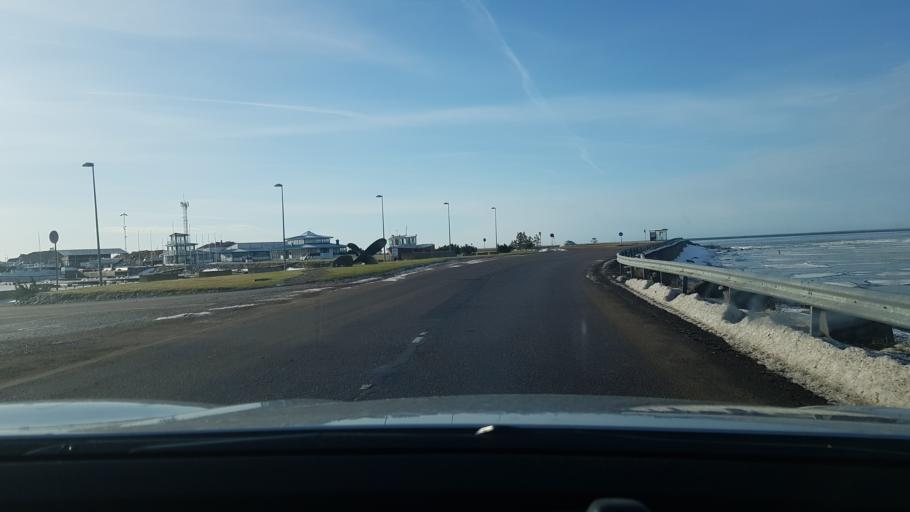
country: EE
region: Saare
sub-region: Kuressaare linn
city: Kuressaare
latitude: 58.2183
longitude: 22.5054
